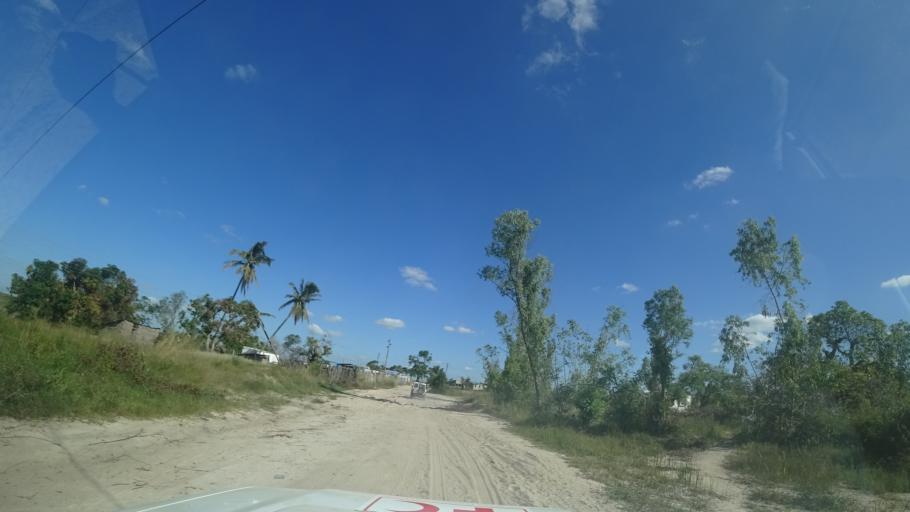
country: MZ
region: Sofala
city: Dondo
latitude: -19.5062
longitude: 34.6100
